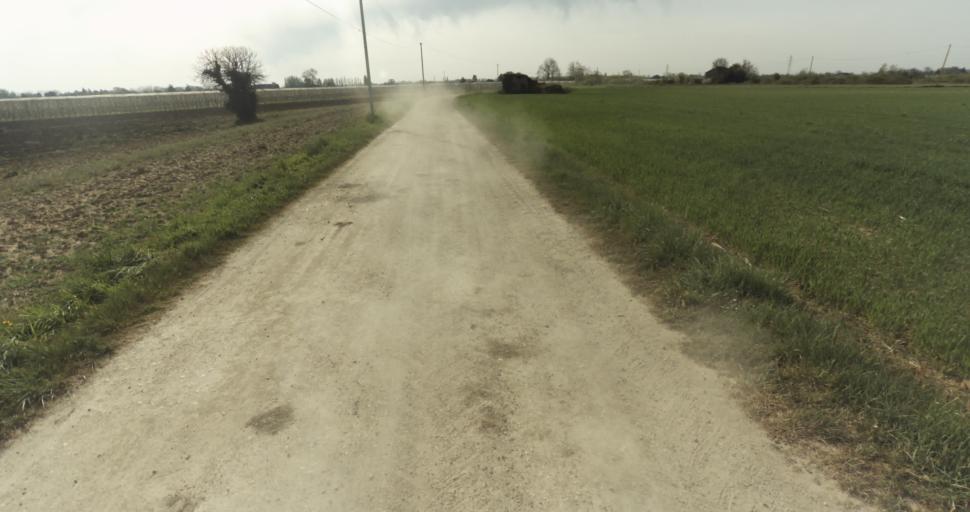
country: FR
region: Midi-Pyrenees
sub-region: Departement du Tarn-et-Garonne
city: Moissac
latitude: 44.1145
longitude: 1.1311
